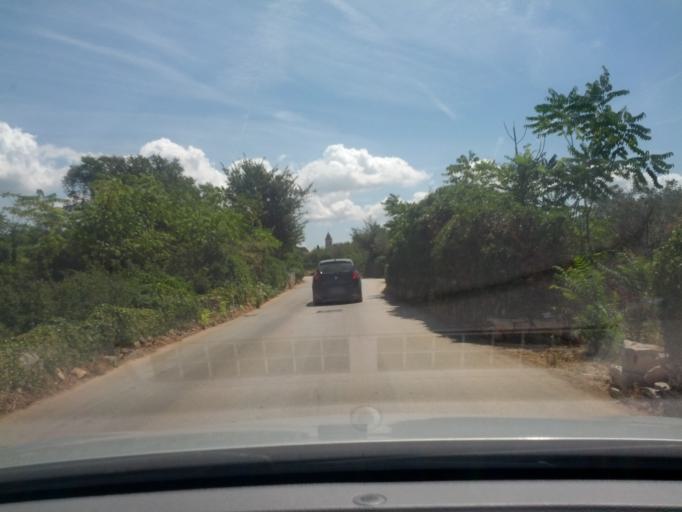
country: HR
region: Istarska
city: Fazana
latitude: 44.9532
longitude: 13.7924
